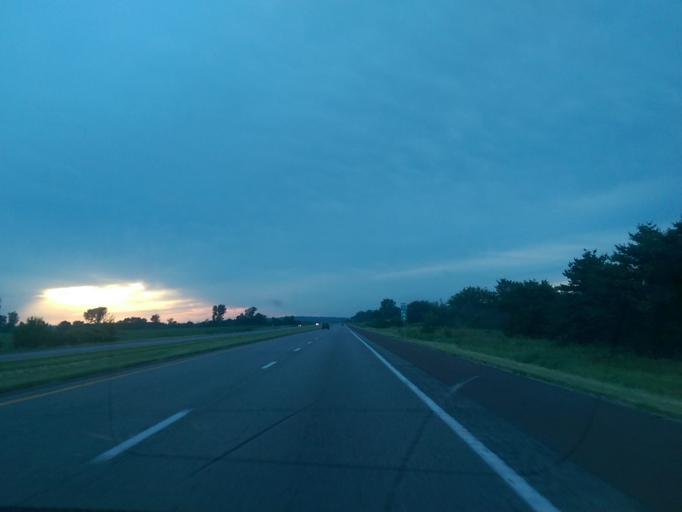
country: US
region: Missouri
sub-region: Holt County
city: Mound City
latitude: 40.1726
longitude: -95.3017
